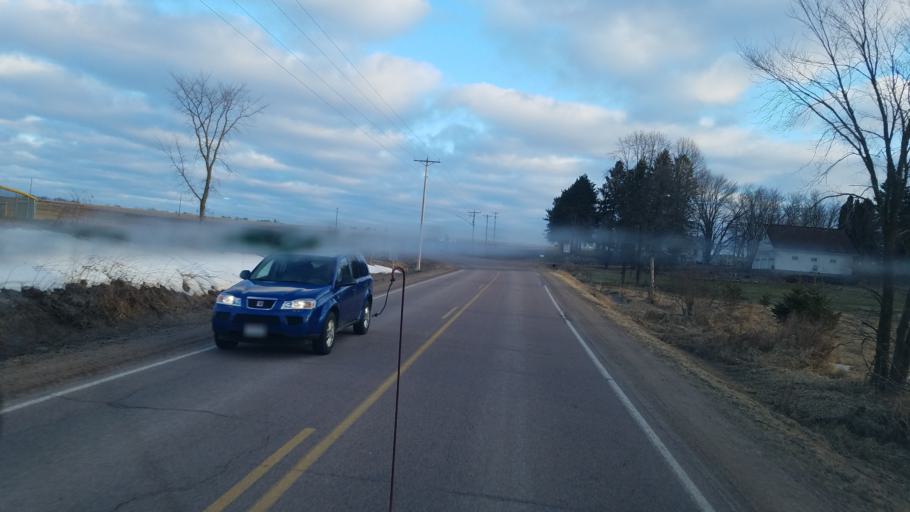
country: US
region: Wisconsin
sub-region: Clark County
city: Neillsville
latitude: 44.5945
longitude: -90.4616
